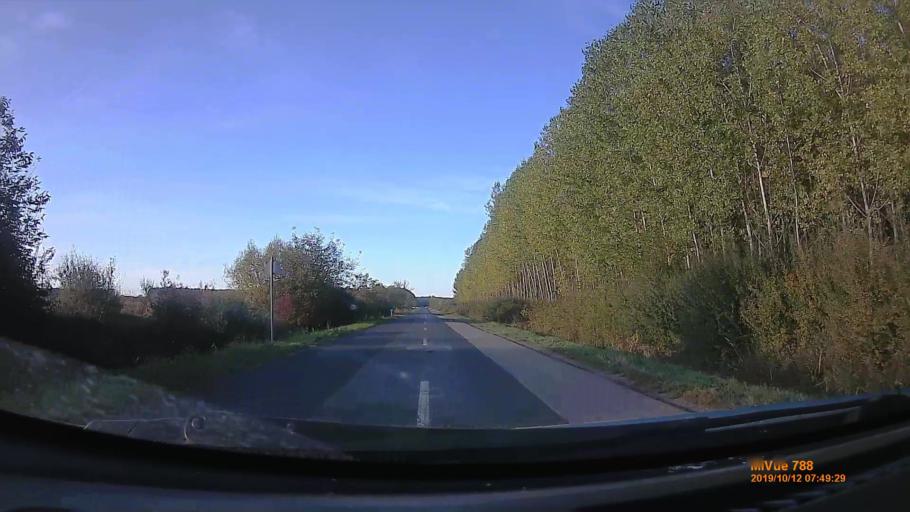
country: HU
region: Hajdu-Bihar
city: Biharkeresztes
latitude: 47.1623
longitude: 21.7449
